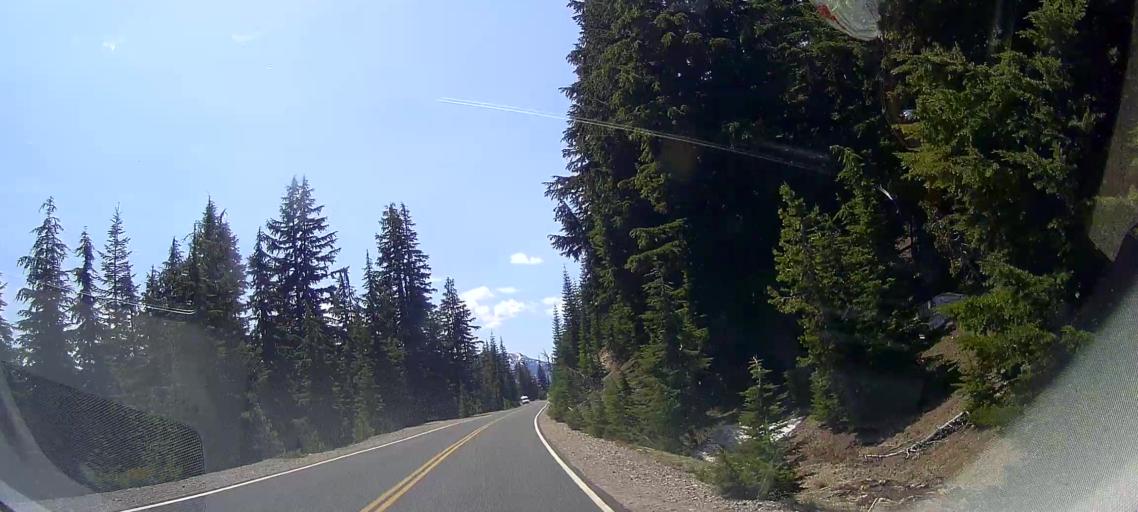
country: US
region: Oregon
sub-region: Jackson County
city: Shady Cove
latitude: 42.9802
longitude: -122.1071
